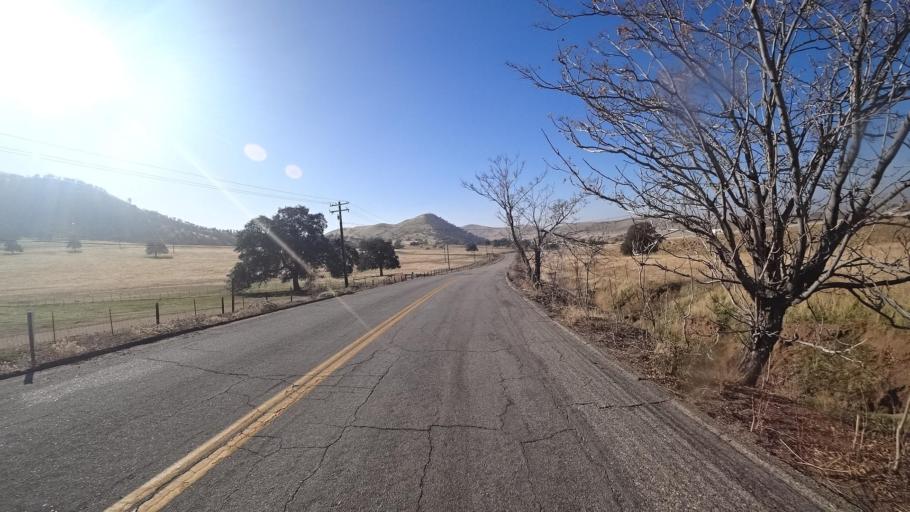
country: US
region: California
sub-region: Kern County
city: Bear Valley Springs
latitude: 35.2619
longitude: -118.6374
